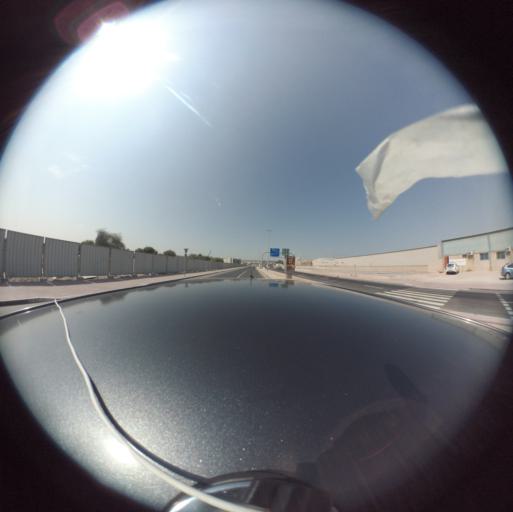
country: AE
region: Dubai
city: Dubai
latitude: 25.1619
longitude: 55.2385
